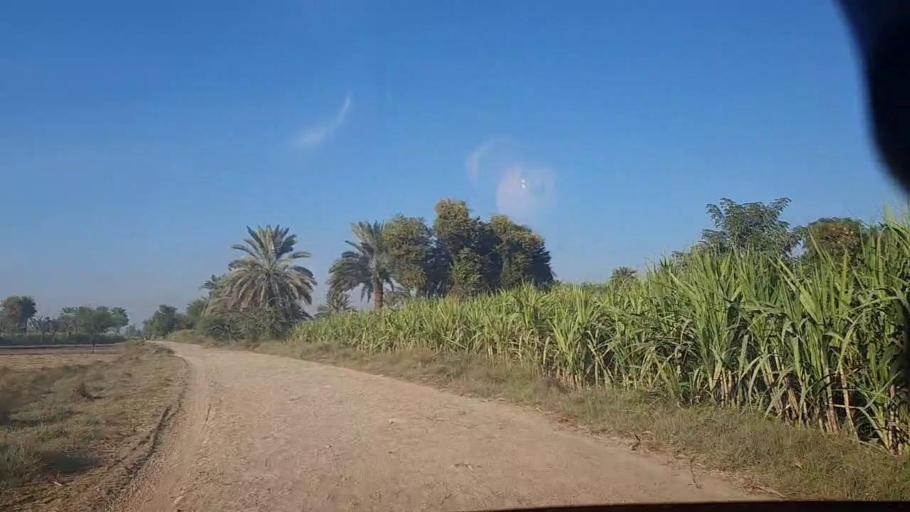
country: PK
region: Sindh
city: Sobhadero
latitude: 27.3925
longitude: 68.4201
